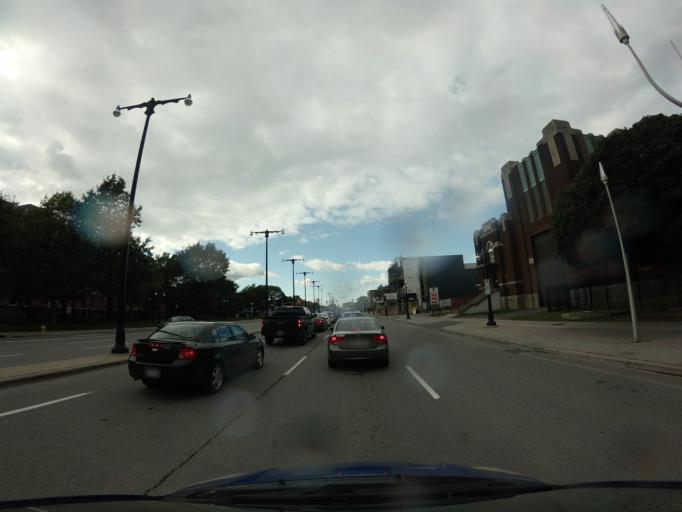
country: CA
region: Ontario
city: Ottawa
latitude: 45.4297
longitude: -75.6864
